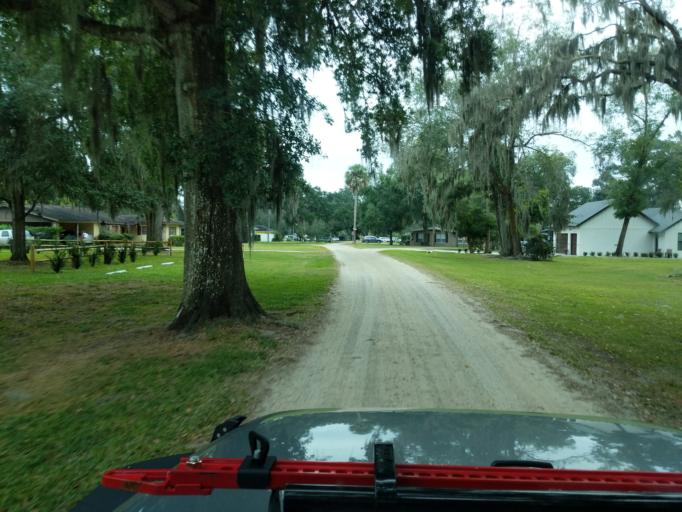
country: US
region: Florida
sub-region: Orange County
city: Oakland
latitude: 28.5568
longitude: -81.6255
